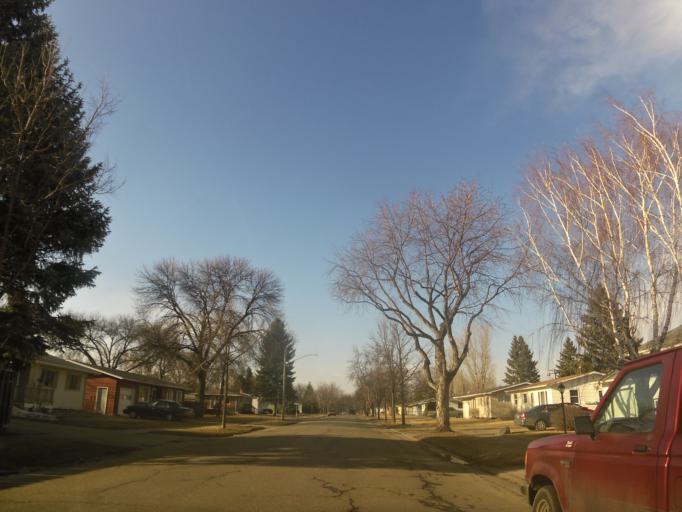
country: US
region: North Dakota
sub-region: Grand Forks County
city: Grand Forks
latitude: 47.9005
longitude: -97.0511
